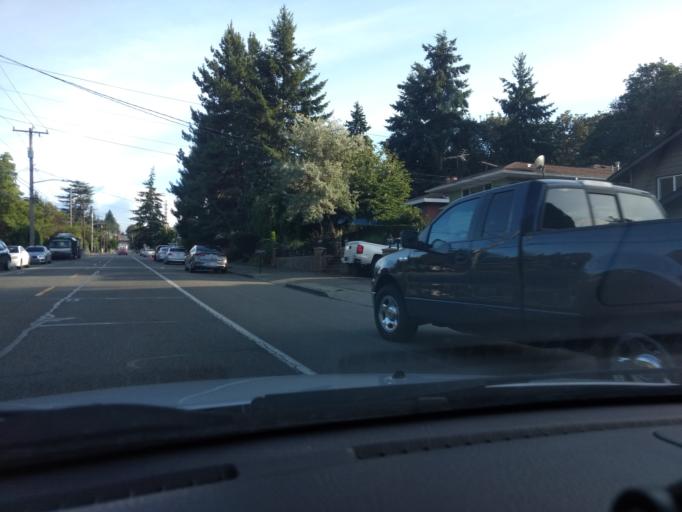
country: US
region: Washington
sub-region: King County
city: Bryn Mawr-Skyway
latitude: 47.5111
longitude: -122.2701
